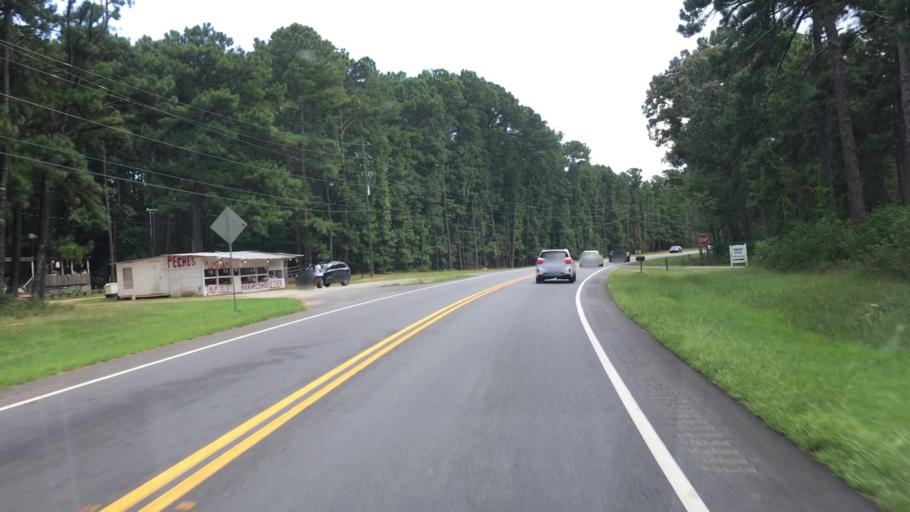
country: US
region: Georgia
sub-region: Putnam County
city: Jefferson
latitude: 33.4063
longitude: -83.3679
